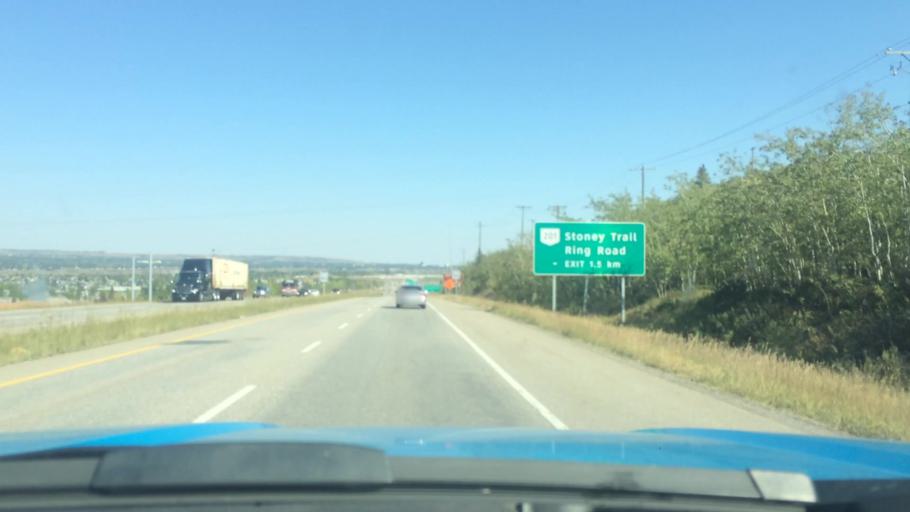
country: CA
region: Alberta
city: Calgary
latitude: 51.0885
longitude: -114.2606
